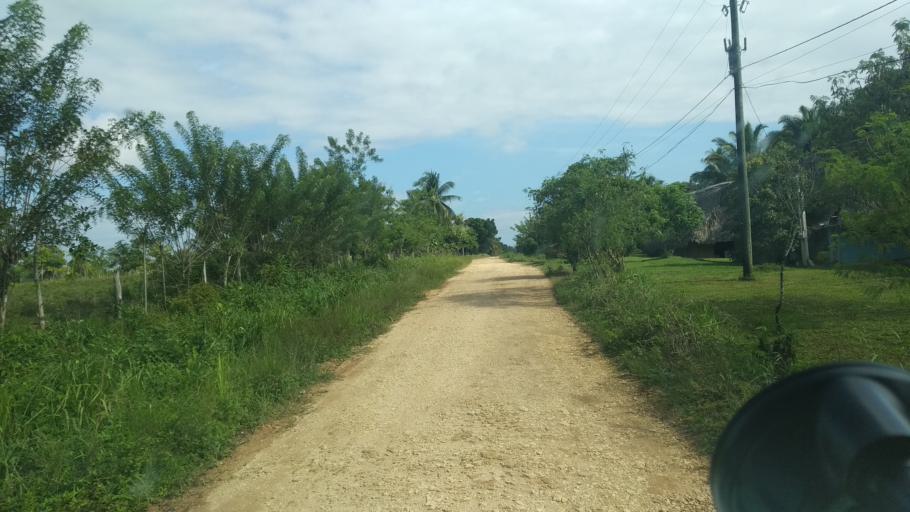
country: BZ
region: Toledo
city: Punta Gorda
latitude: 16.2101
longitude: -88.9127
